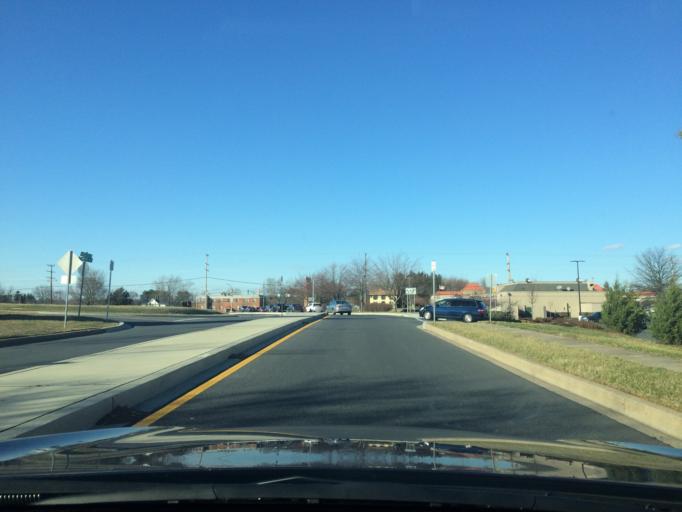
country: US
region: Maryland
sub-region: Carroll County
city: Eldersburg
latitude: 39.3982
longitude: -76.9358
